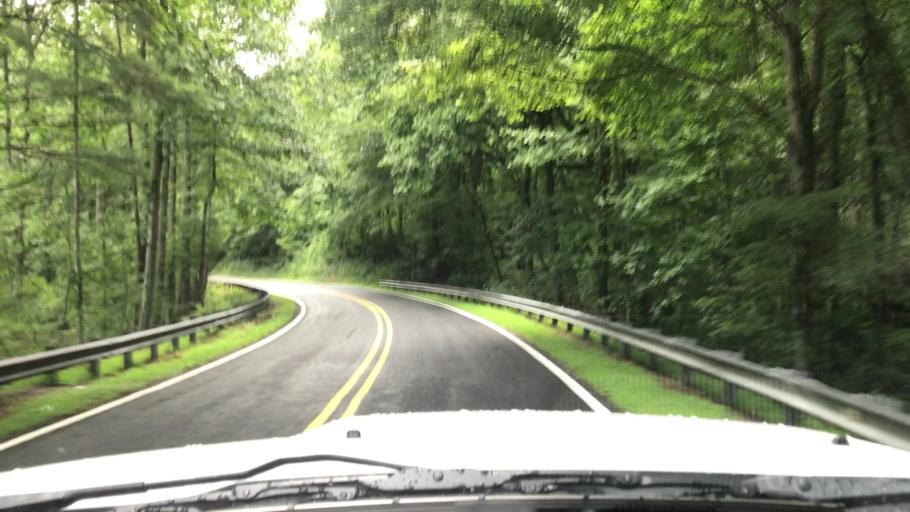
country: US
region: North Carolina
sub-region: Graham County
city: Robbinsville
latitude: 35.3681
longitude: -83.8534
